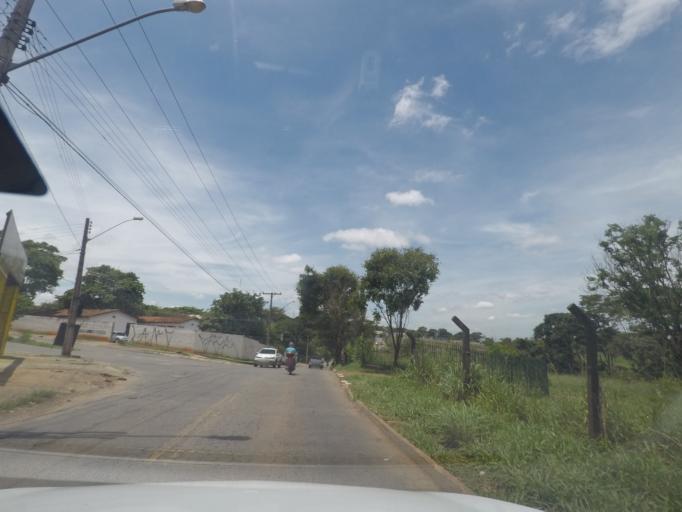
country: BR
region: Goias
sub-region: Goiania
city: Goiania
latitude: -16.6537
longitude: -49.2036
